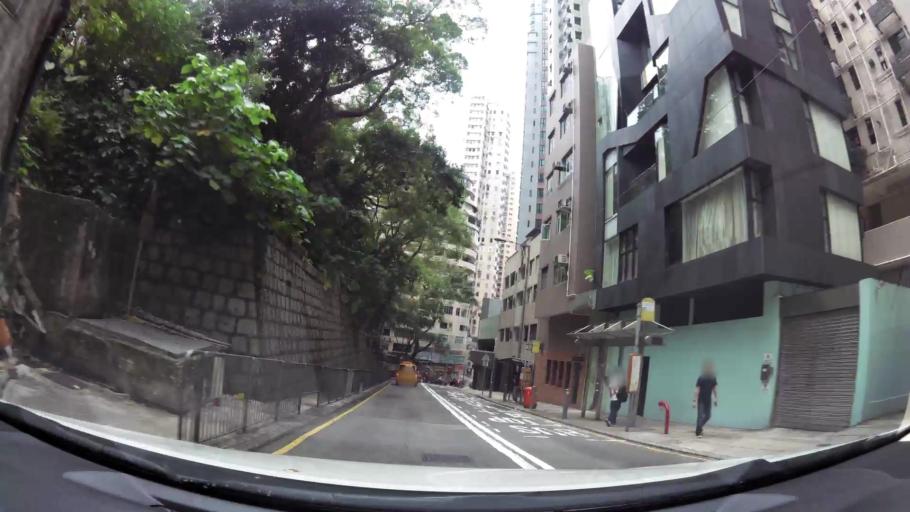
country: HK
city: Hong Kong
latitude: 22.2837
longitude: 114.1437
